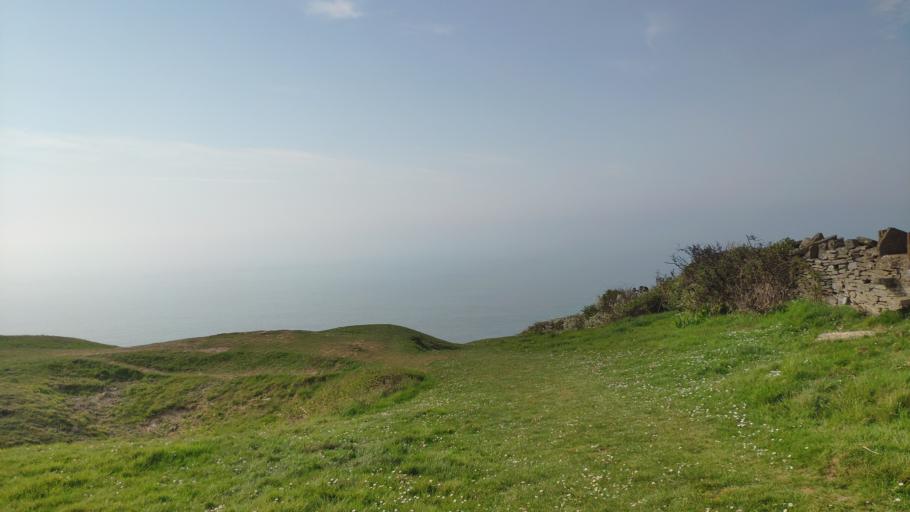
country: GB
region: England
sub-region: Dorset
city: Swanage
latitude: 50.5931
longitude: -1.9726
